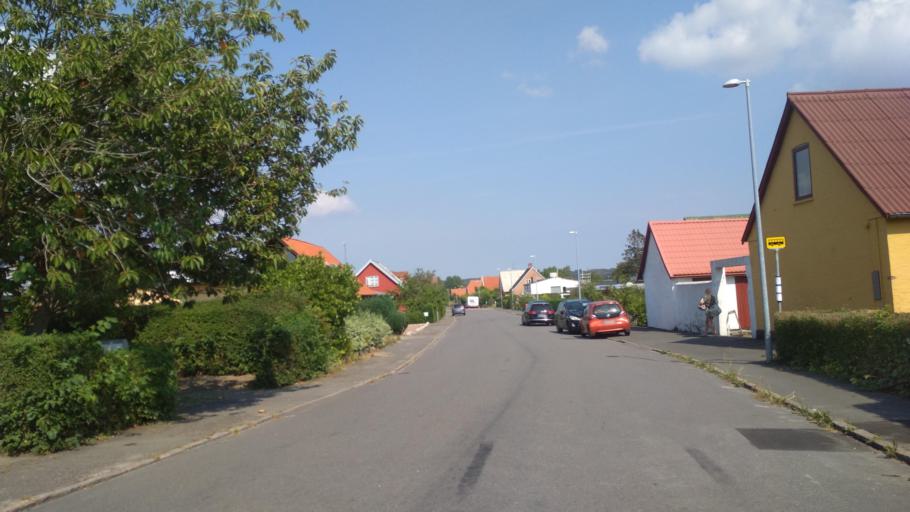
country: DK
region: Capital Region
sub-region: Bornholm Kommune
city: Akirkeby
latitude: 55.0677
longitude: 14.9261
